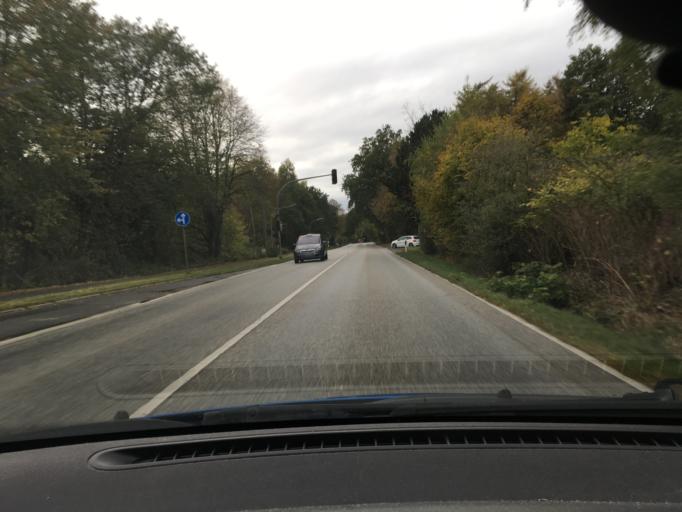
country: DE
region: Schleswig-Holstein
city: Hohenhorn
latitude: 53.4898
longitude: 10.3512
